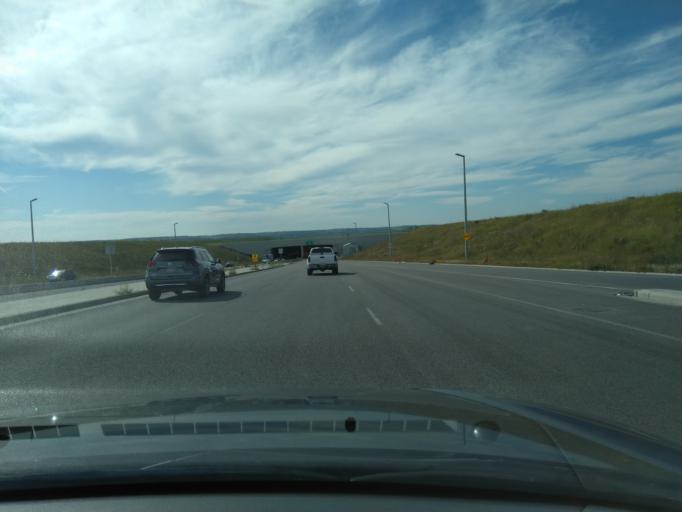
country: CA
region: Alberta
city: Calgary
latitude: 51.1399
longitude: -113.9825
